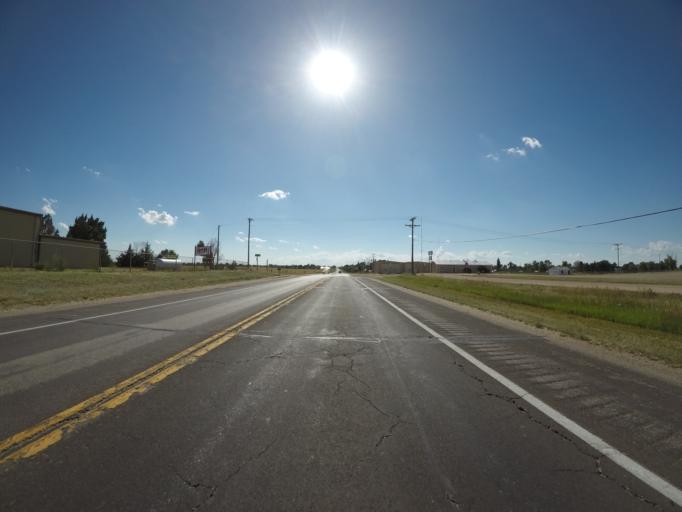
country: US
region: Colorado
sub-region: Logan County
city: Sterling
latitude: 40.6238
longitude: -103.2861
